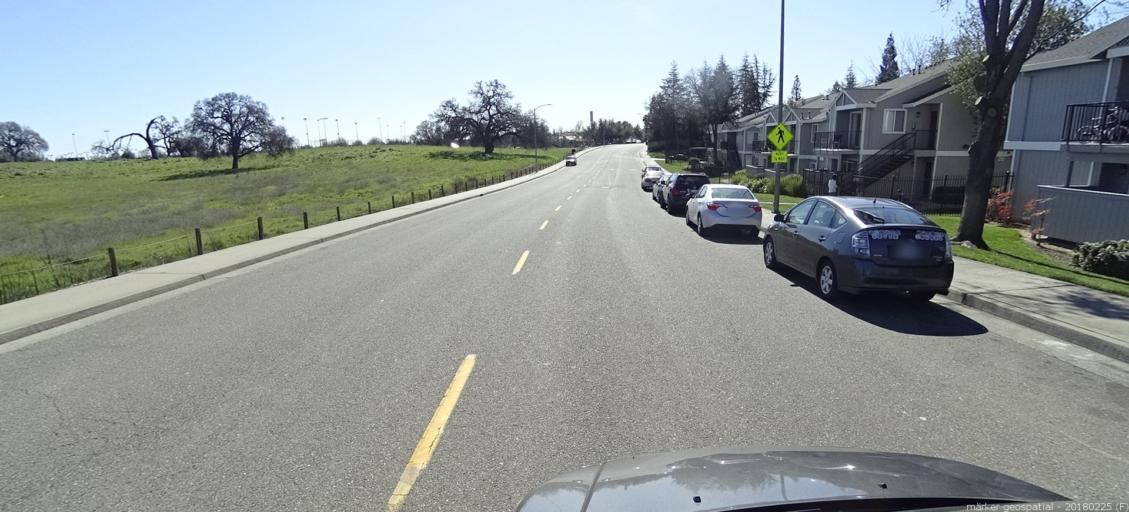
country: US
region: California
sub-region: Sacramento County
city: Antelope
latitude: 38.7161
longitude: -121.3591
